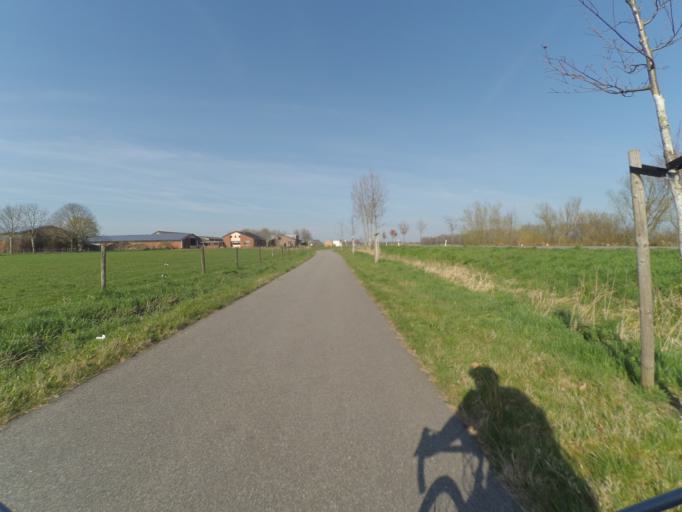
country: NL
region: Gelderland
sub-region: Gemeente Groesbeek
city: De Horst
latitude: 51.8129
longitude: 5.9691
